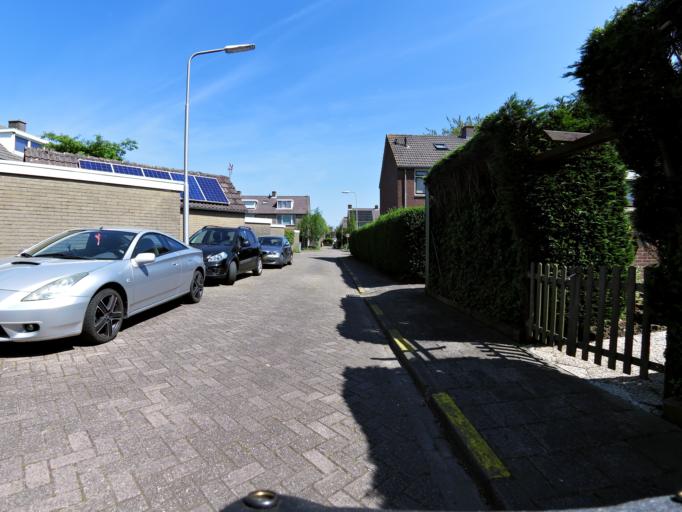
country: NL
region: South Holland
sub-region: Gemeente Binnenmaas
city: Heinenoord
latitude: 51.8284
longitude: 4.4792
